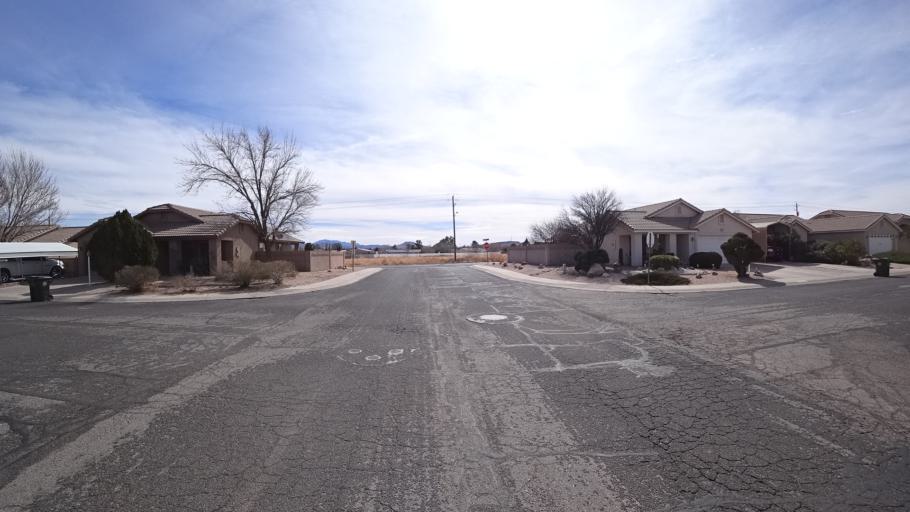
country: US
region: Arizona
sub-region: Mohave County
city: New Kingman-Butler
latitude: 35.2327
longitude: -114.0309
